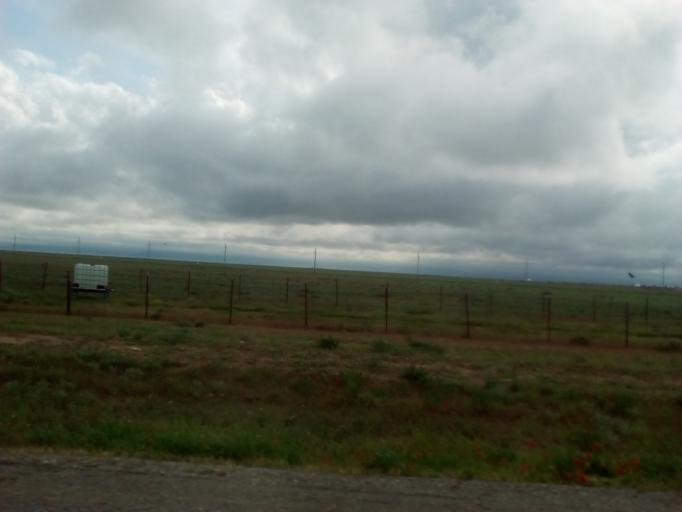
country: KZ
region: Ongtustik Qazaqstan
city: Sholaqqkorghan
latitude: 43.7455
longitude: 69.2002
